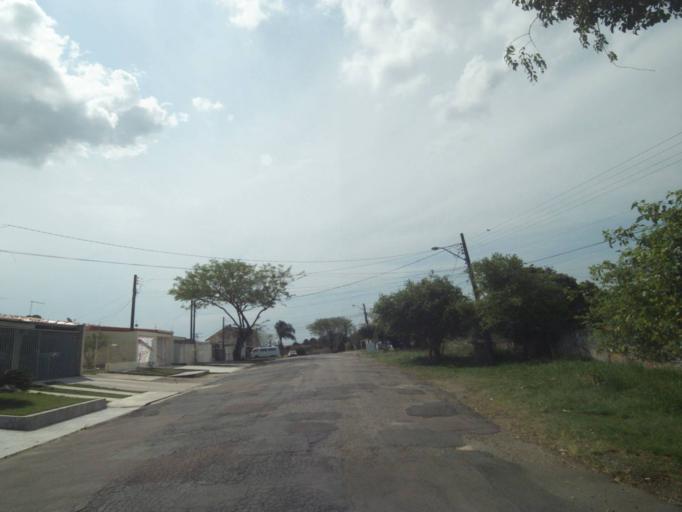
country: BR
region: Parana
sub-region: Pinhais
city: Pinhais
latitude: -25.4048
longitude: -49.2112
